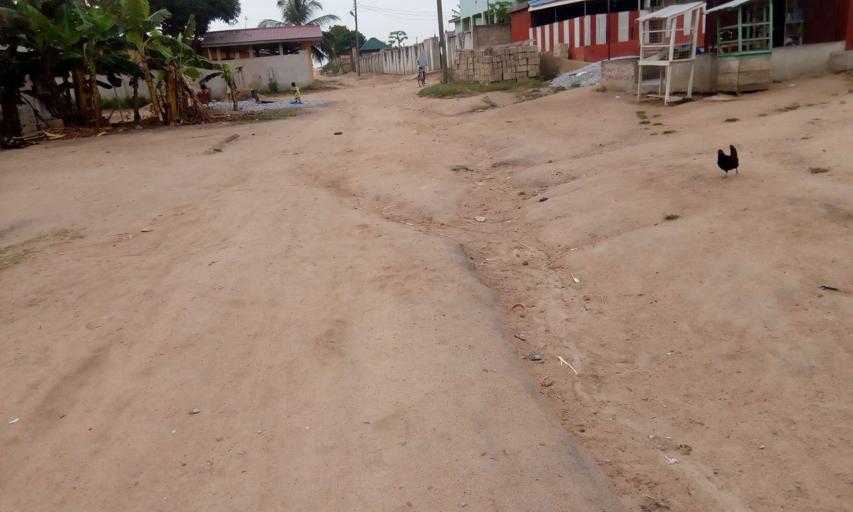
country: GH
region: Central
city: Winneba
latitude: 5.3562
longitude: -0.6216
